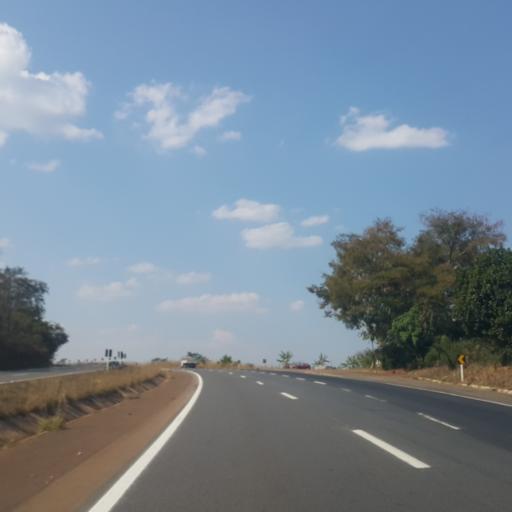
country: BR
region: Goias
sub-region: Abadiania
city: Abadiania
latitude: -16.2962
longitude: -48.8029
